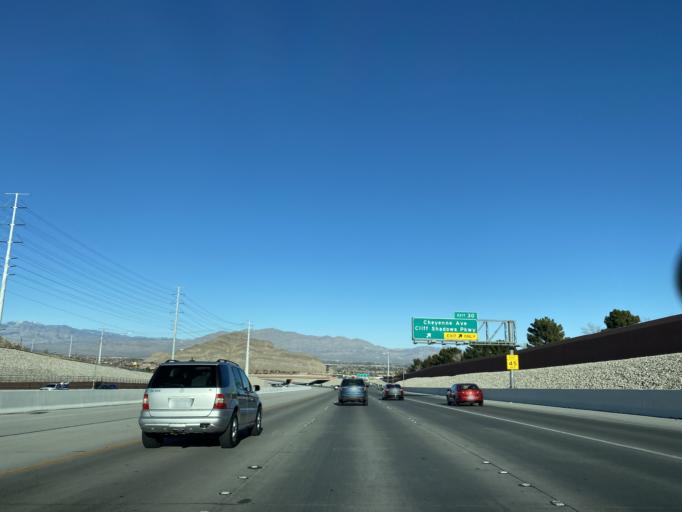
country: US
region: Nevada
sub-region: Clark County
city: Summerlin South
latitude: 36.2149
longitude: -115.3315
